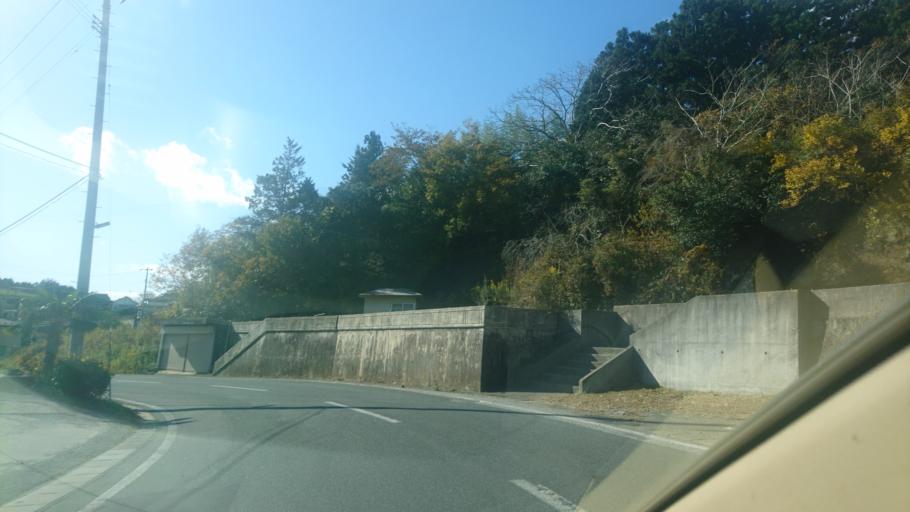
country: JP
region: Iwate
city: Ofunato
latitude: 38.9940
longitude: 141.7261
